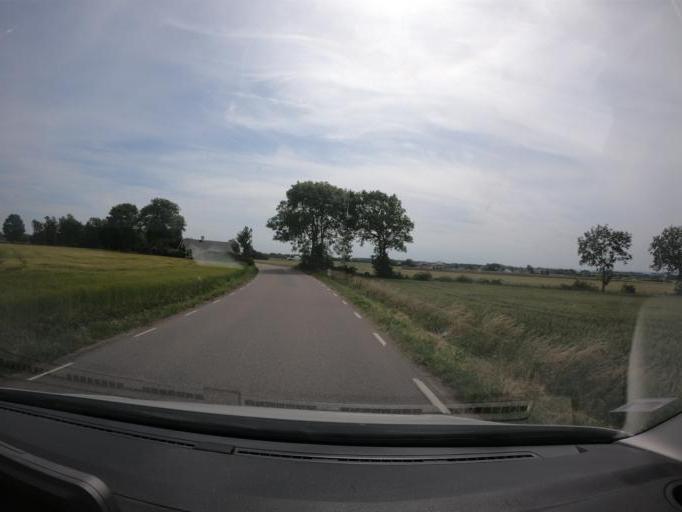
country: SE
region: Skane
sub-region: Bastads Kommun
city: Forslov
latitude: 56.3590
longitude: 12.7796
